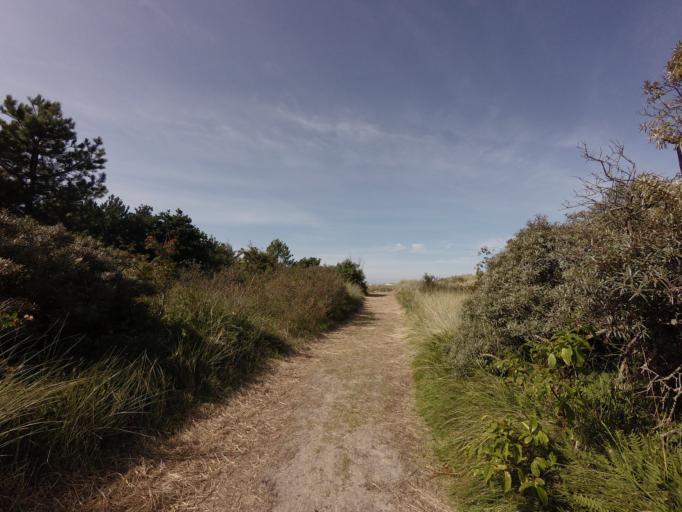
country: NL
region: Friesland
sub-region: Gemeente Ameland
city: Nes
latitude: 53.4554
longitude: 5.7683
